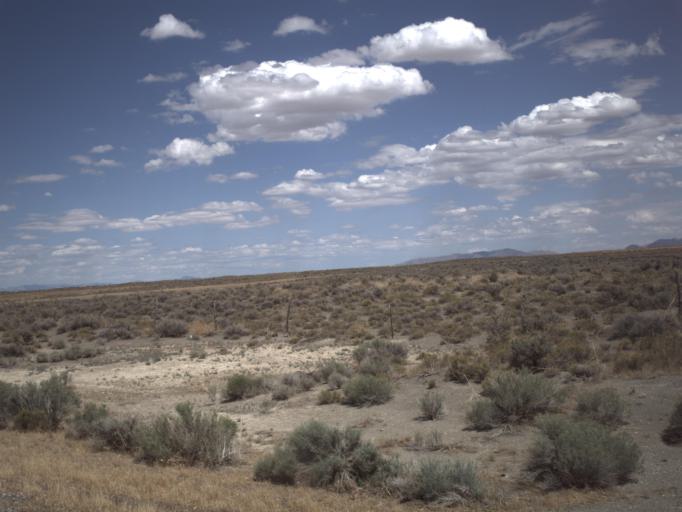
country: US
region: Utah
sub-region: Millard County
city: Delta
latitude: 39.2951
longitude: -112.4687
